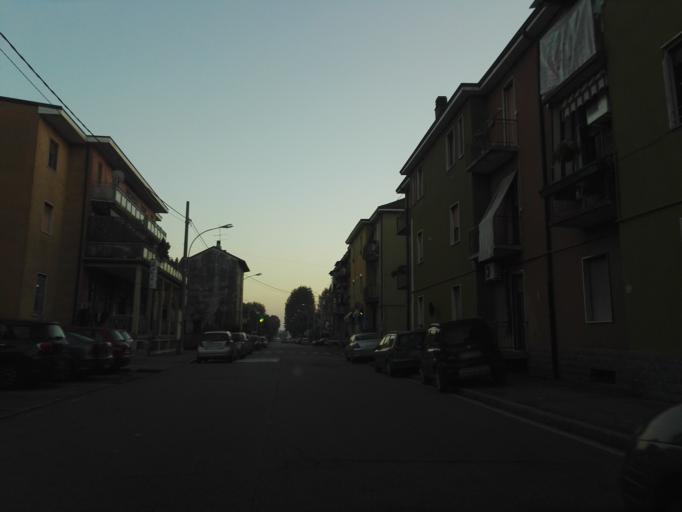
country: IT
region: Lombardy
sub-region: Citta metropolitana di Milano
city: Mezzate
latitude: 45.4458
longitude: 9.2940
